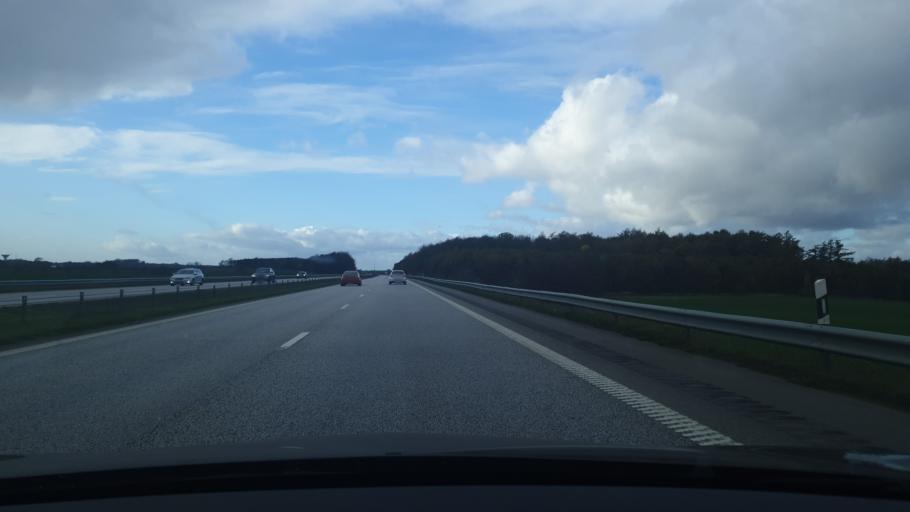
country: SE
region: Skane
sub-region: Malmo
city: Oxie
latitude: 55.5445
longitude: 13.1505
